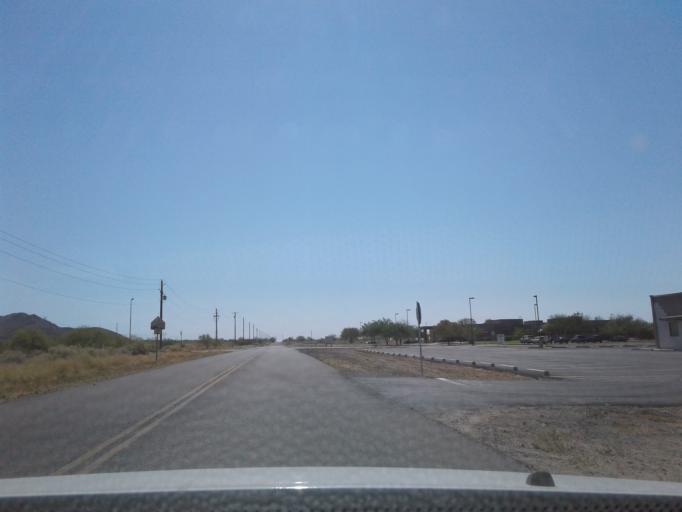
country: US
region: Arizona
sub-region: Maricopa County
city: Laveen
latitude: 33.2904
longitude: -112.1579
